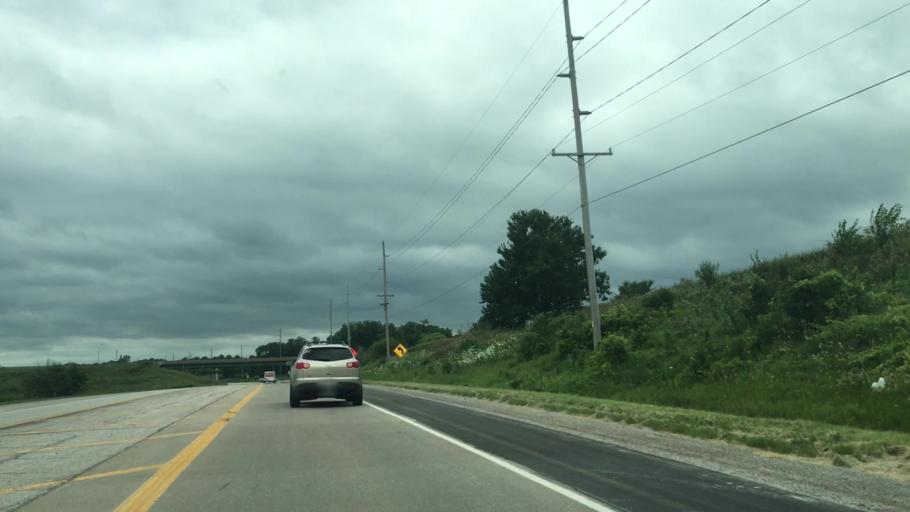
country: US
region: Iowa
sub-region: Johnson County
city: Tiffin
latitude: 41.7044
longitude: -91.6385
